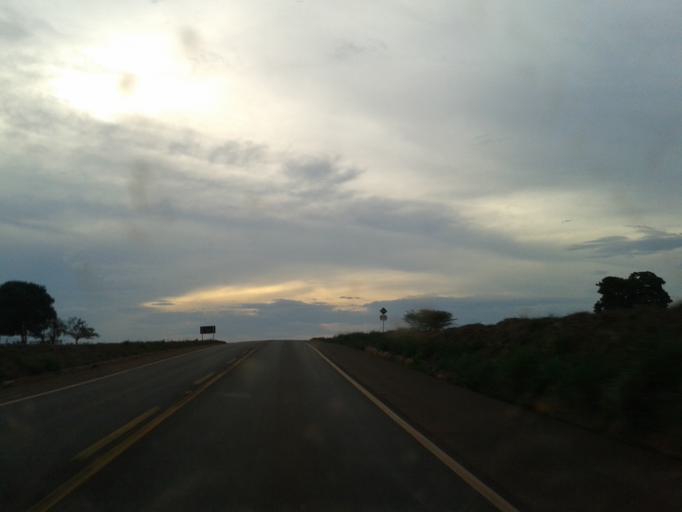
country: BR
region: Goias
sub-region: Santa Helena De Goias
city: Santa Helena de Goias
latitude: -17.8906
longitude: -50.6665
